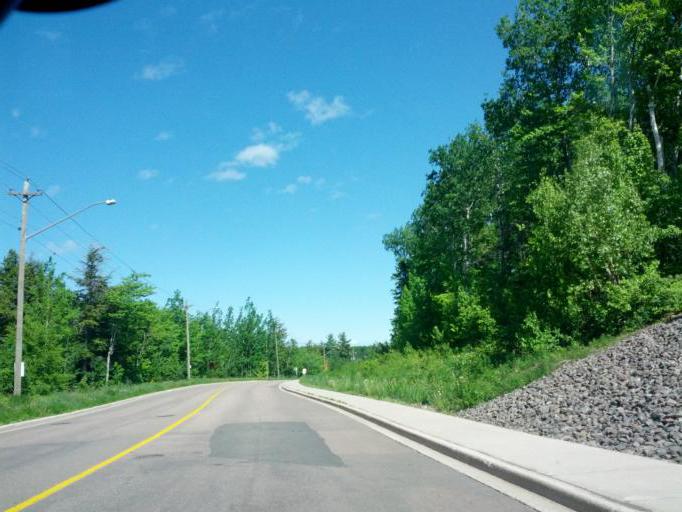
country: CA
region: New Brunswick
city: Moncton
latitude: 46.1219
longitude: -64.8342
